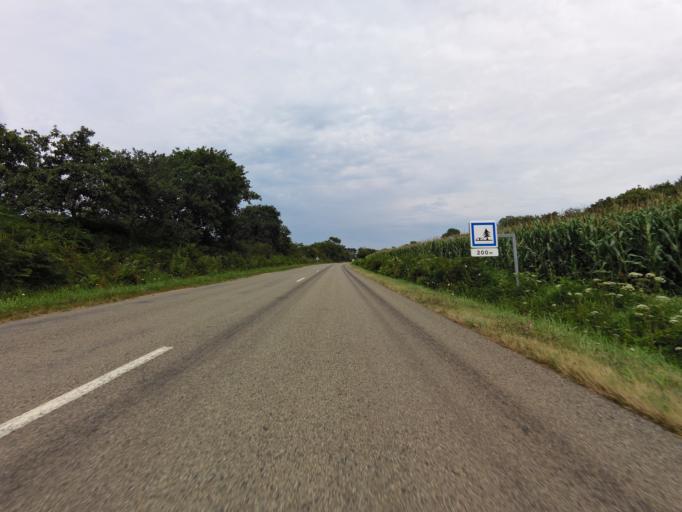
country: FR
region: Brittany
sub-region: Departement du Finistere
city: Poullan-sur-Mer
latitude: 48.0776
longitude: -4.4449
